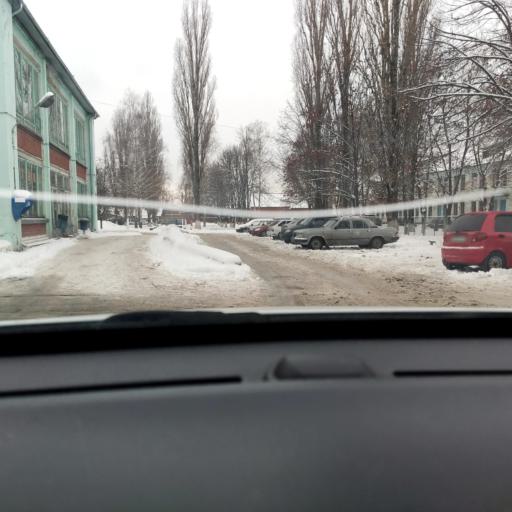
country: RU
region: Voronezj
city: Novaya Usman'
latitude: 51.6483
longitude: 39.4168
